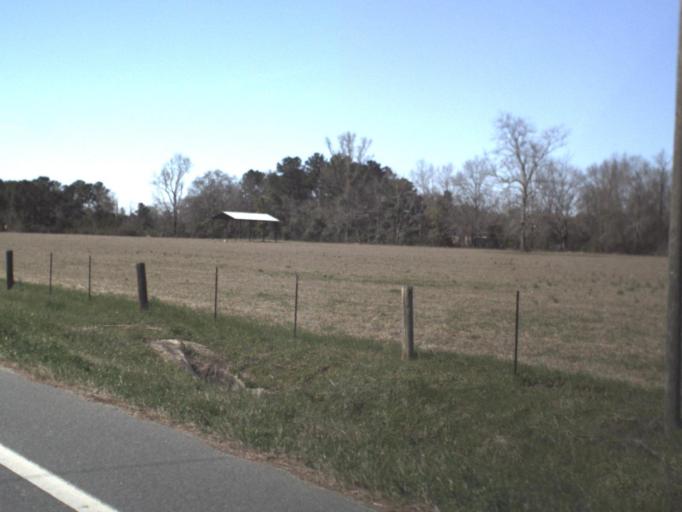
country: US
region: Florida
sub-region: Gadsden County
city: Chattahoochee
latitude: 30.6925
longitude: -84.7367
